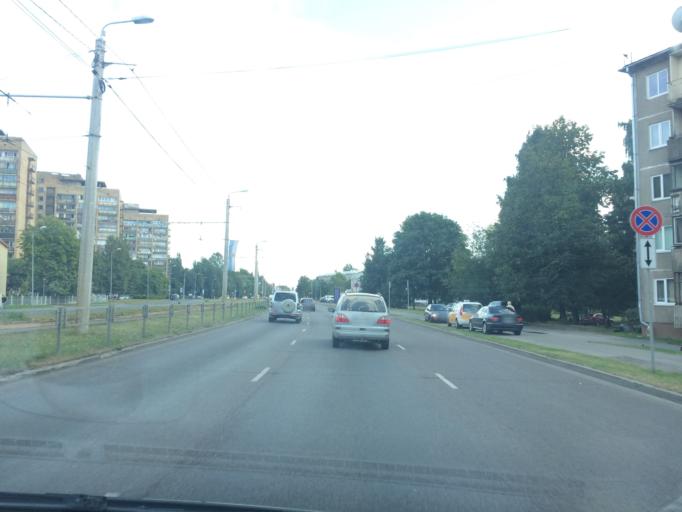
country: LV
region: Kekava
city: Balozi
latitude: 56.9098
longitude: 24.1802
